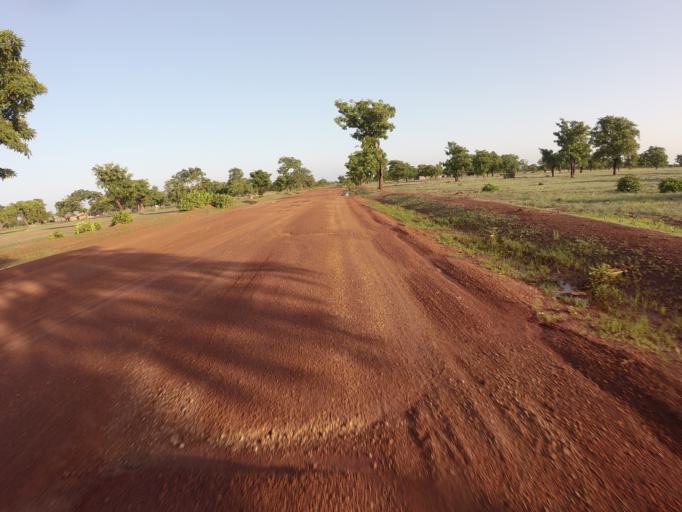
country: TG
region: Savanes
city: Sansanne-Mango
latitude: 10.2783
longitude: -0.0836
